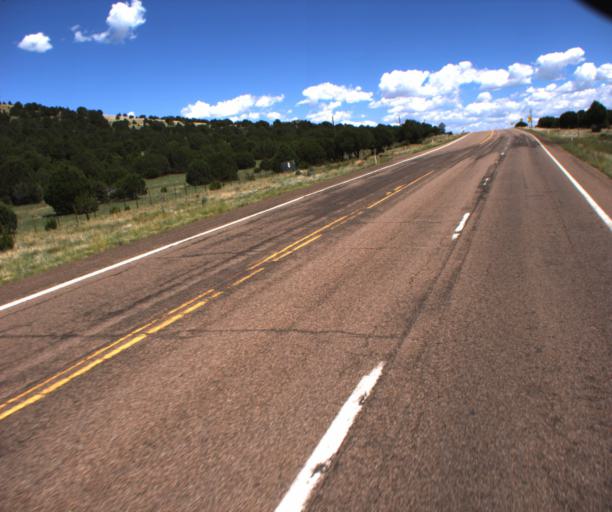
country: US
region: Arizona
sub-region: Apache County
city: Springerville
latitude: 34.2663
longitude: -109.5832
